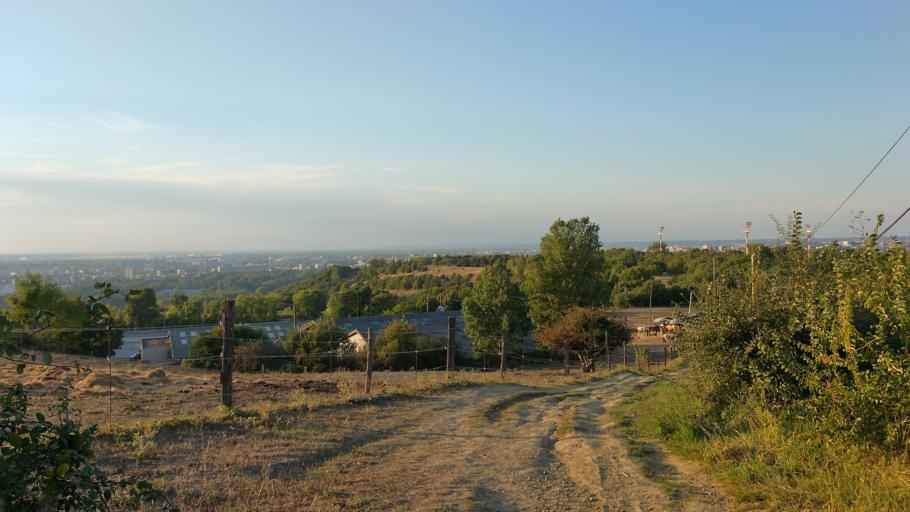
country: FR
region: Midi-Pyrenees
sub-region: Departement de la Haute-Garonne
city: Ramonville-Saint-Agne
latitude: 43.5592
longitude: 1.4466
